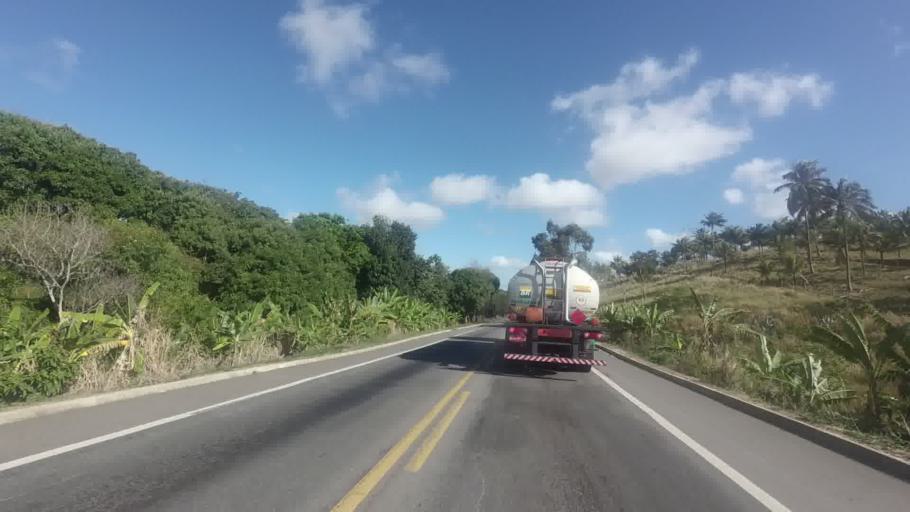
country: BR
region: Espirito Santo
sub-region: Guarapari
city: Guarapari
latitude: -20.5398
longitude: -40.4821
